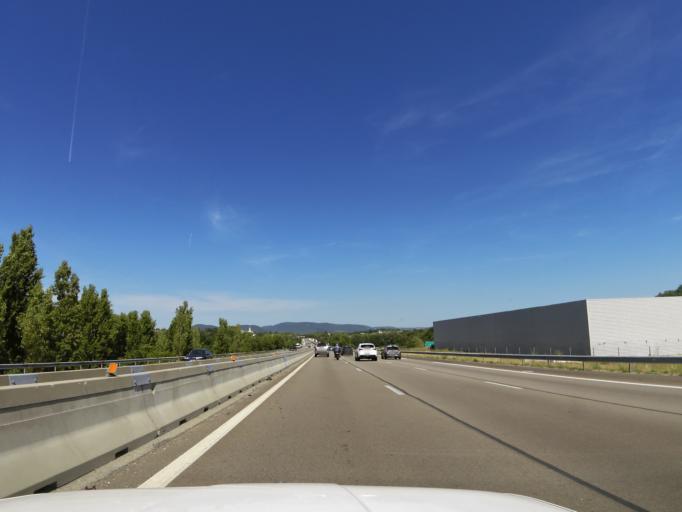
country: FR
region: Rhone-Alpes
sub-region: Departement de la Drome
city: Montboucher-sur-Jabron
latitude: 44.5383
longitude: 4.8050
